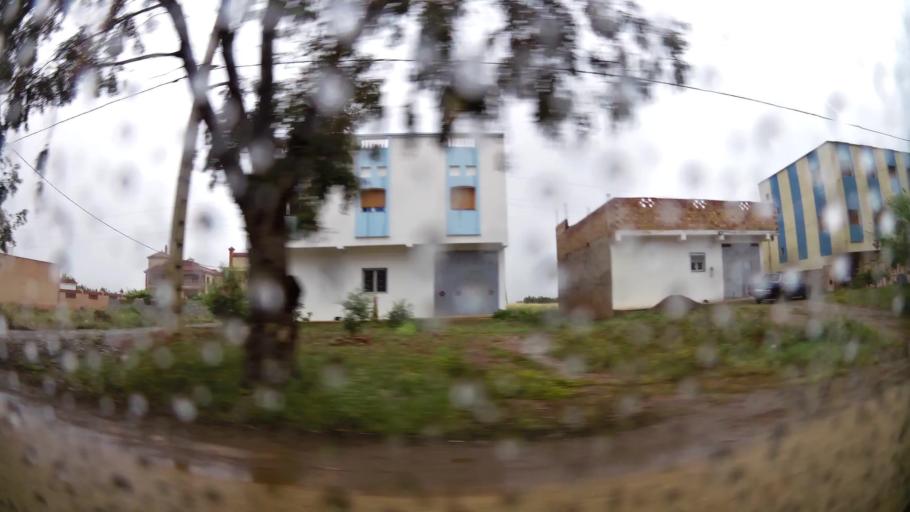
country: MA
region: Oriental
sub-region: Nador
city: Boudinar
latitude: 35.1252
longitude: -3.6468
